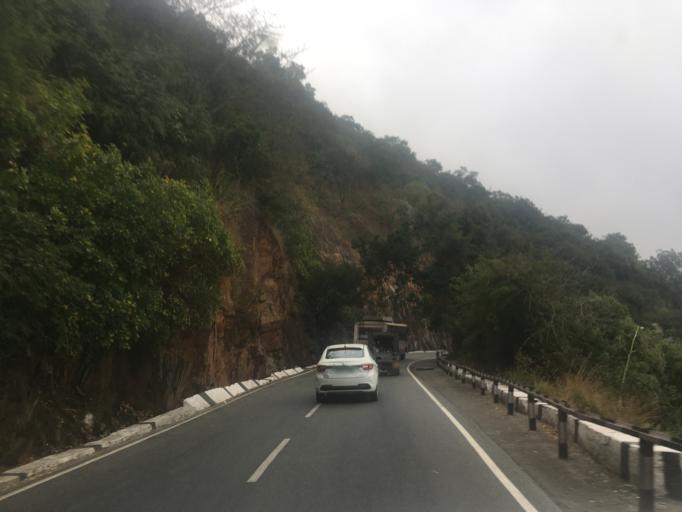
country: IN
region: Andhra Pradesh
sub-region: Chittoor
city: Tirumala
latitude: 13.6678
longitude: 79.3491
